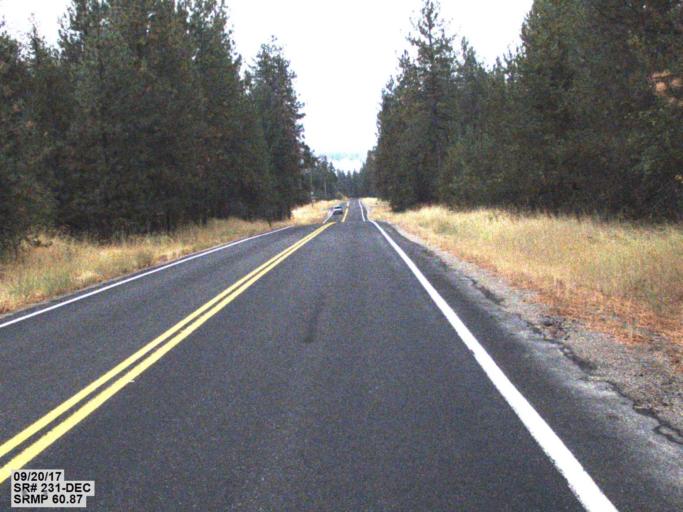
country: US
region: Washington
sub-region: Stevens County
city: Chewelah
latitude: 48.0392
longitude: -117.7365
